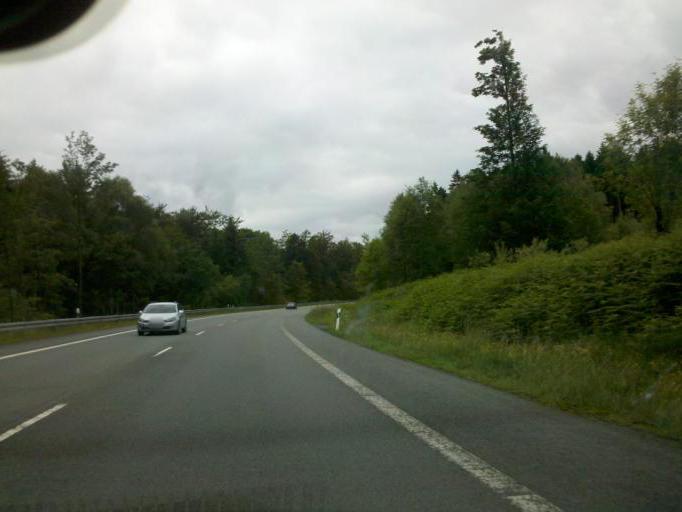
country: DE
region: North Rhine-Westphalia
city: Warstein
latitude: 51.4125
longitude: 8.3253
